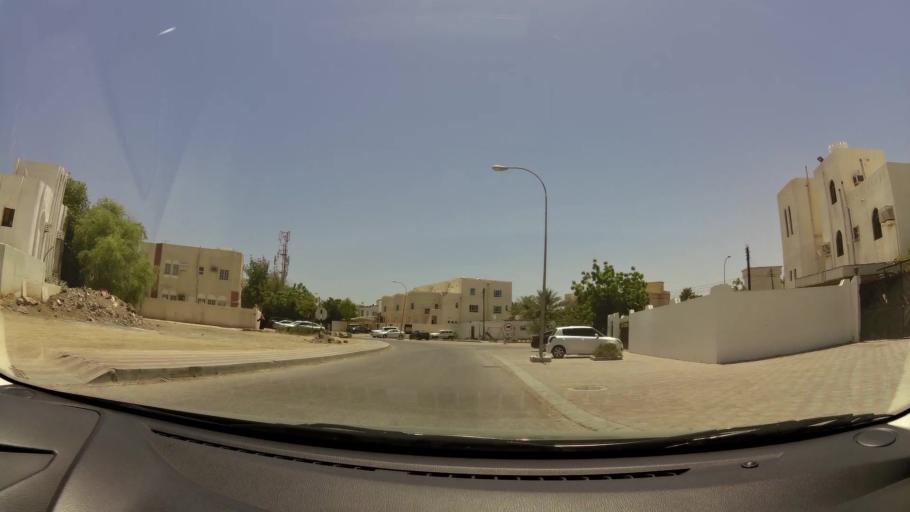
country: OM
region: Muhafazat Masqat
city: As Sib al Jadidah
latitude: 23.6245
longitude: 58.2408
